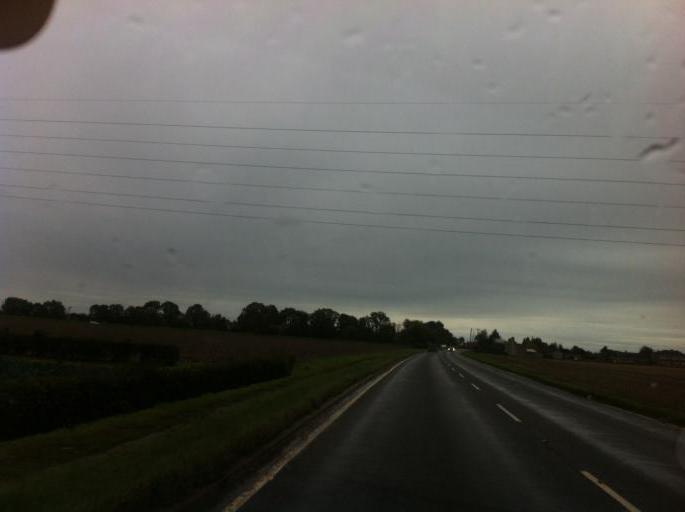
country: GB
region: England
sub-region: Lincolnshire
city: Boston
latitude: 52.9850
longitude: 0.0273
